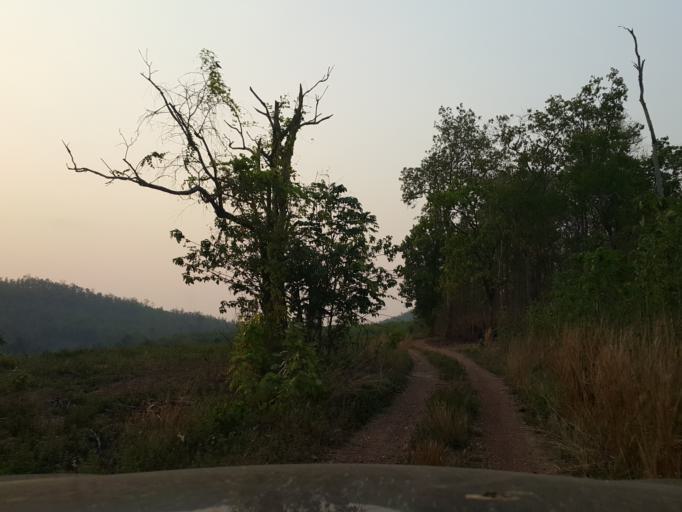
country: TH
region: Lamphun
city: Thung Hua Chang
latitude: 17.9145
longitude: 99.0738
